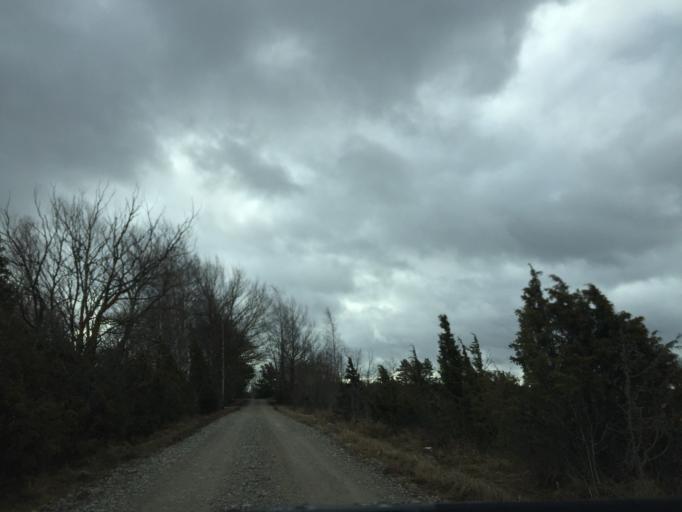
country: EE
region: Laeaene
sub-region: Haapsalu linn
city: Haapsalu
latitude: 58.6860
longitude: 23.5047
